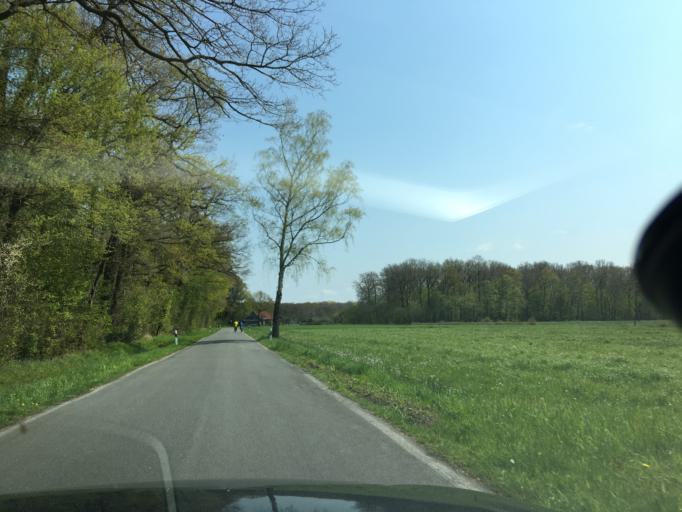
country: DE
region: North Rhine-Westphalia
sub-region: Regierungsbezirk Munster
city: Senden
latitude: 51.8521
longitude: 7.5394
